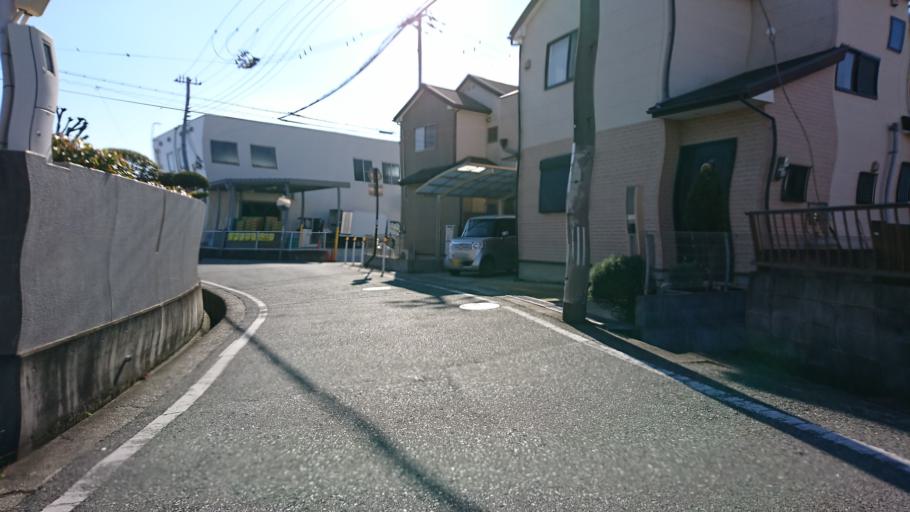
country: JP
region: Hyogo
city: Kakogawacho-honmachi
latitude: 34.7327
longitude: 134.8455
